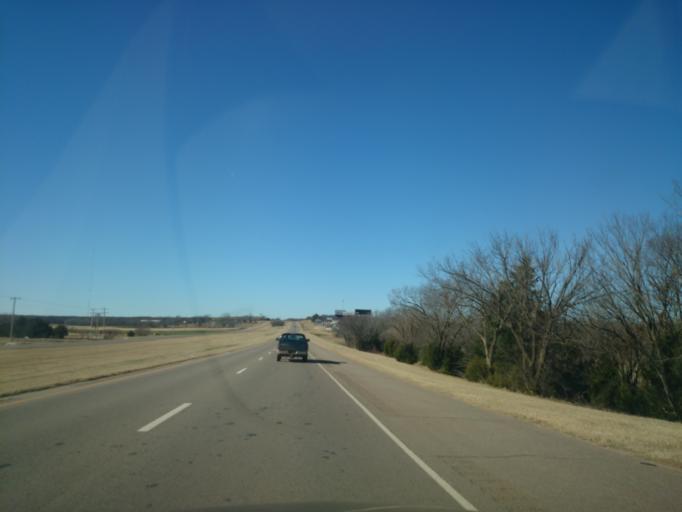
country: US
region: Oklahoma
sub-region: Payne County
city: Stillwater
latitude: 36.1163
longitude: -97.1695
